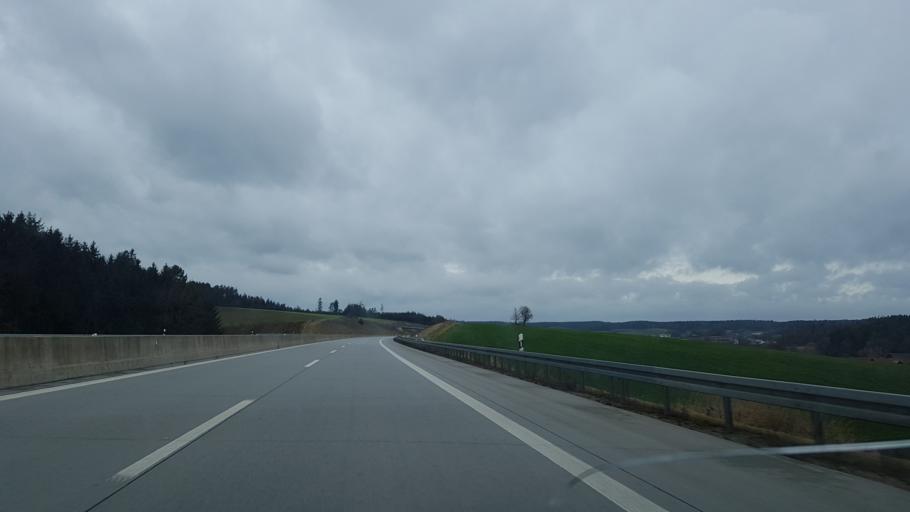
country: DE
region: Bavaria
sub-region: Lower Bavaria
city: Ergoldsbach
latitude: 48.7404
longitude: 12.1482
